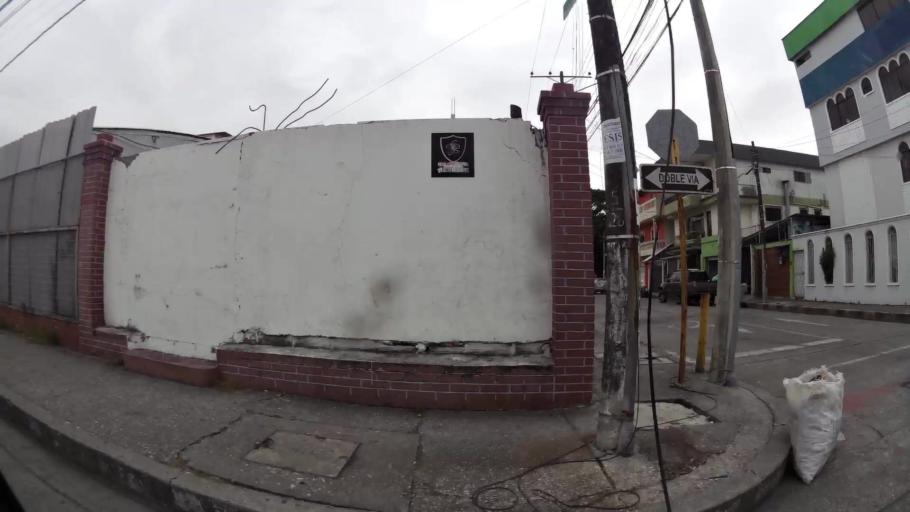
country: EC
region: Guayas
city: Eloy Alfaro
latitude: -2.1525
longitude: -79.8934
